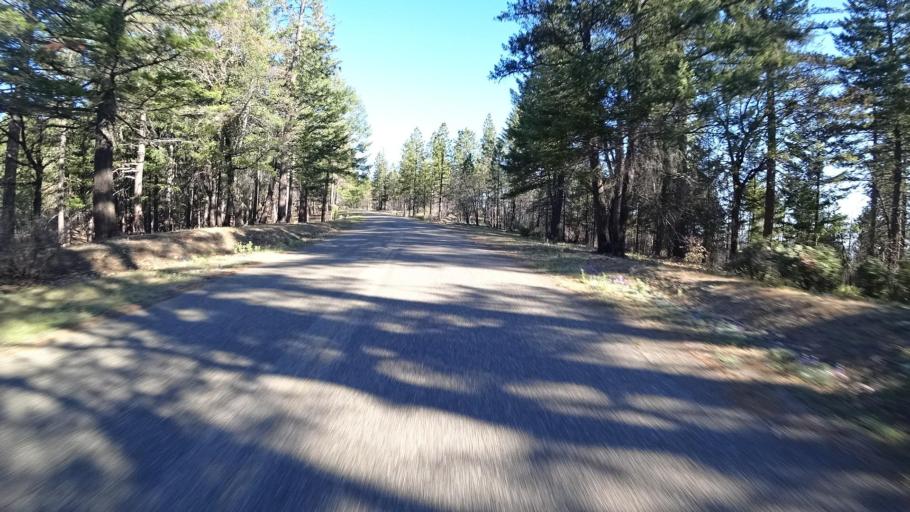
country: US
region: California
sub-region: Lake County
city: Upper Lake
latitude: 39.3068
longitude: -122.9361
